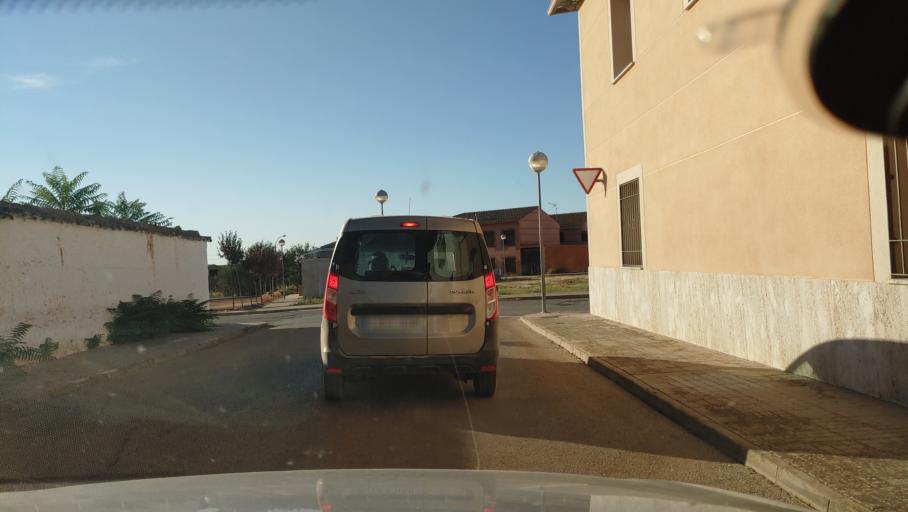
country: ES
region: Castille-La Mancha
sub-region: Provincia de Ciudad Real
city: Infantes
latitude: 38.7402
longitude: -3.0118
